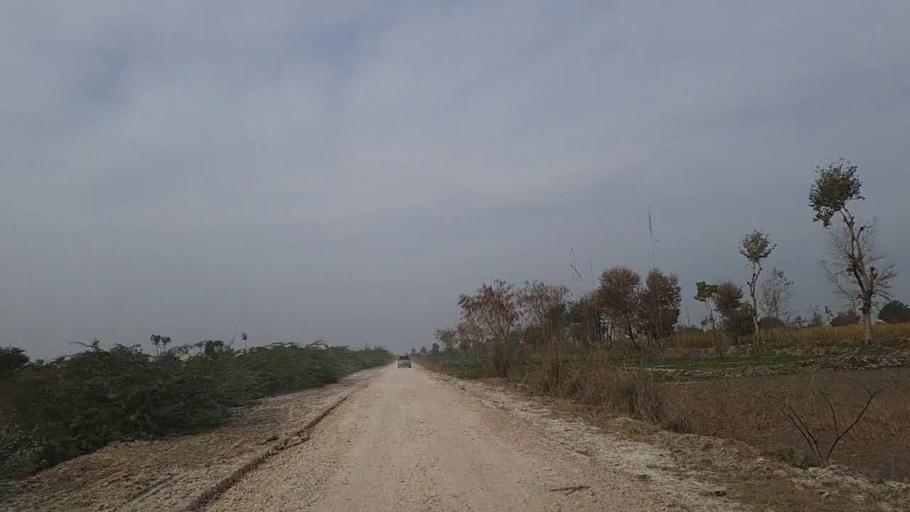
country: PK
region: Sindh
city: Daur
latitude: 26.4100
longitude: 68.4323
